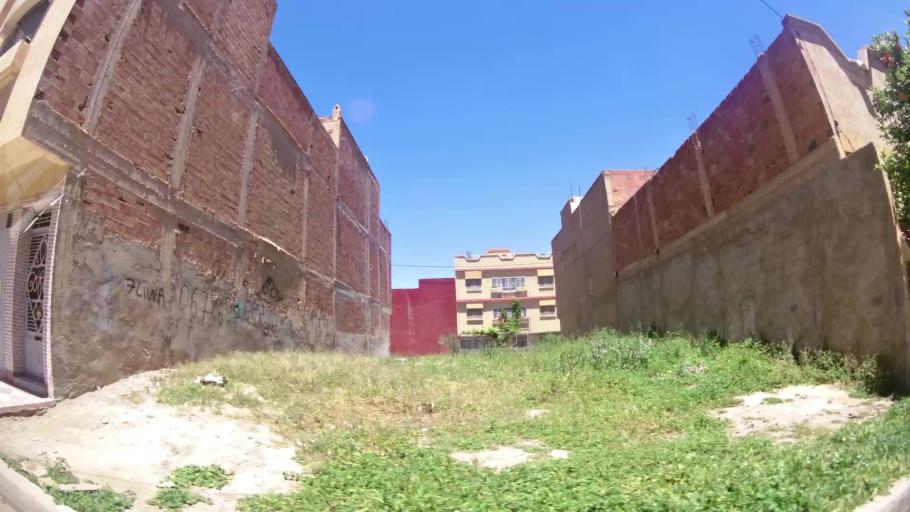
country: MA
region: Oriental
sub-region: Oujda-Angad
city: Oujda
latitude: 34.6769
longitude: -1.8655
